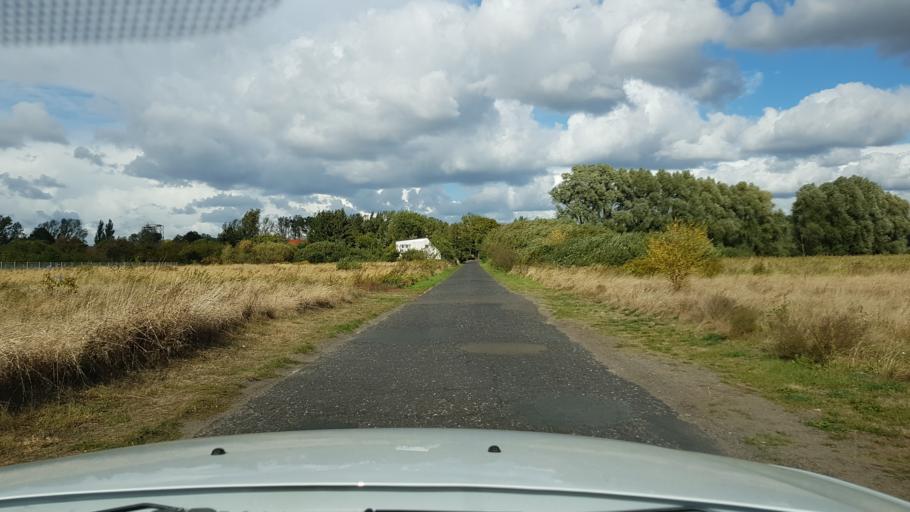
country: PL
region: West Pomeranian Voivodeship
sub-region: Powiat gryfinski
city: Gryfino
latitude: 53.2777
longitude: 14.4954
